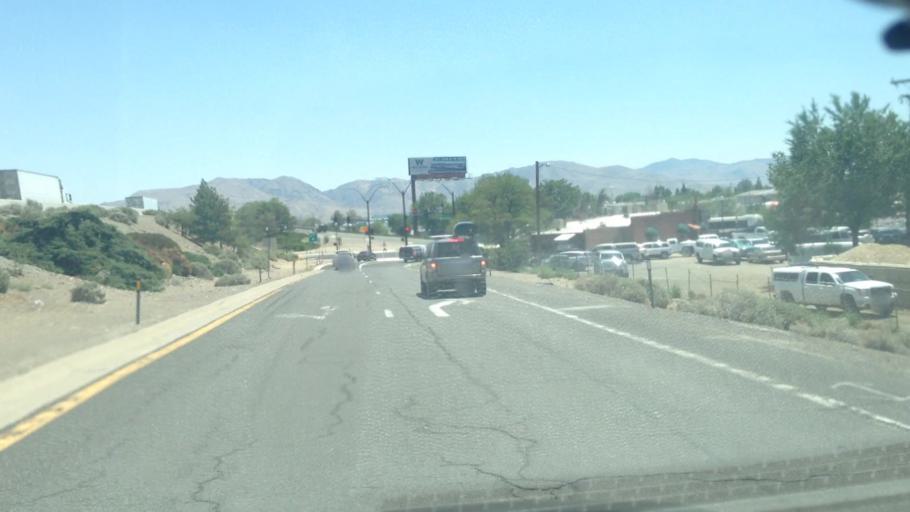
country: US
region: Nevada
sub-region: Washoe County
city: Sparks
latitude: 39.5362
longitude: -119.7810
